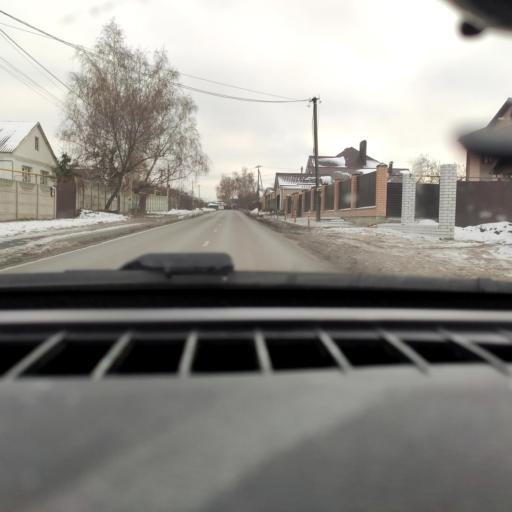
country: RU
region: Voronezj
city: Podgornoye
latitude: 51.7996
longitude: 39.1440
